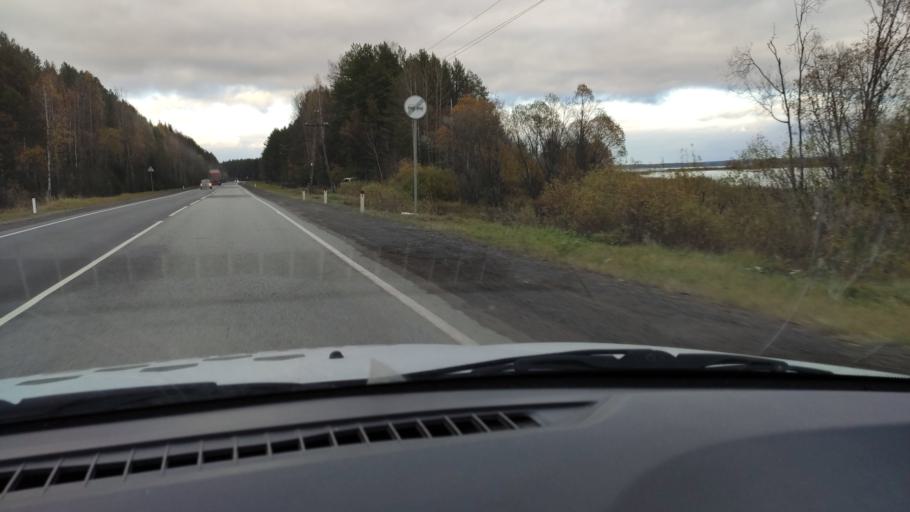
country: RU
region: Kirov
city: Belaya Kholunitsa
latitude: 58.8749
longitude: 50.8618
